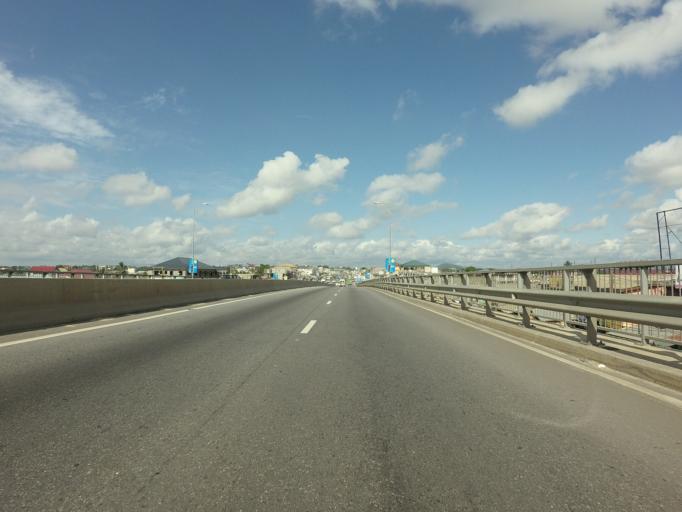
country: GH
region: Central
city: Kasoa
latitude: 5.5343
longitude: -0.4260
